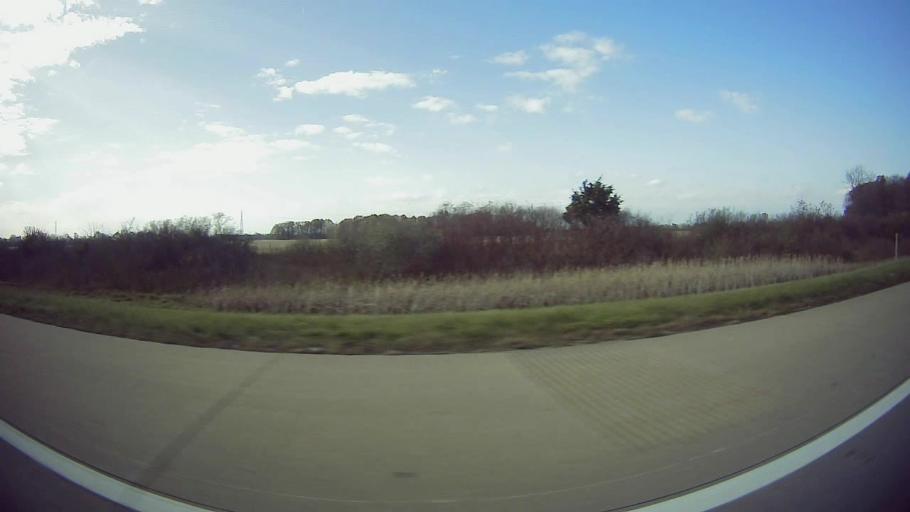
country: US
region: Michigan
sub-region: Monroe County
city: South Rockwood
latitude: 42.0291
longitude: -83.2943
